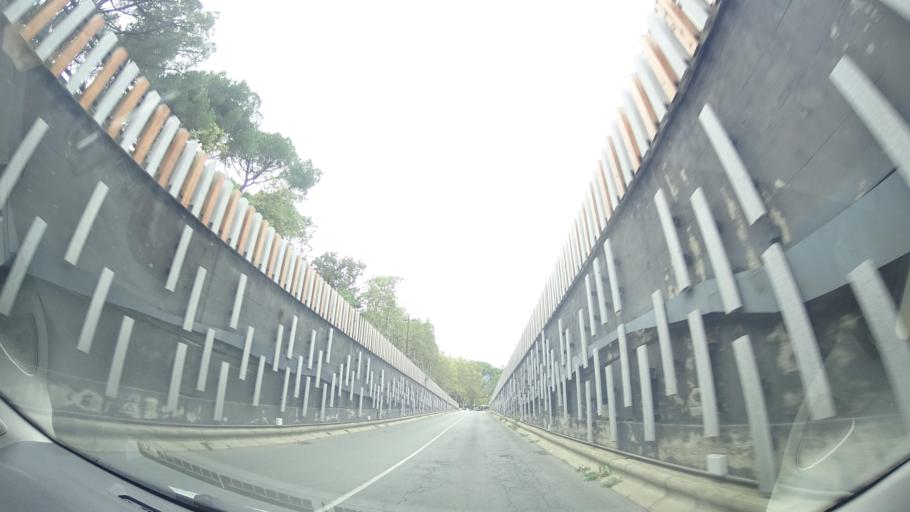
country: ES
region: Madrid
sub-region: Provincia de Madrid
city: El Escorial
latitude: 40.5843
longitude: -4.1330
